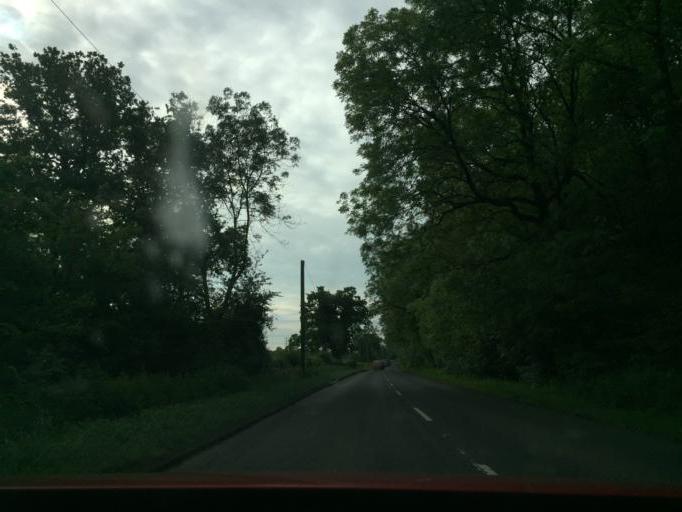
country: GB
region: England
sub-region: Leicestershire
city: Sapcote
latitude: 52.4661
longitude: -1.3034
